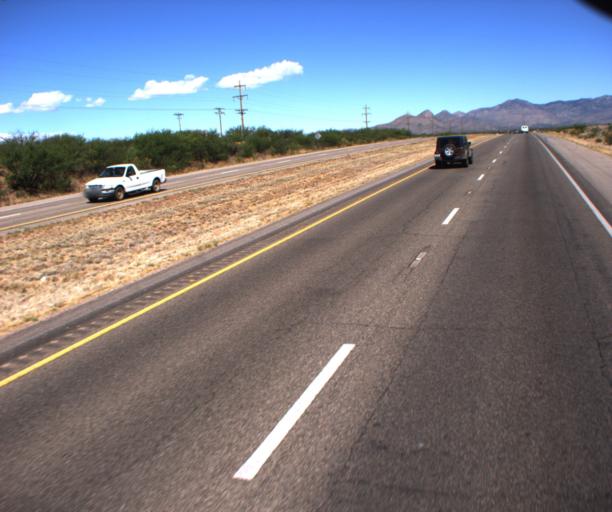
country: US
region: Arizona
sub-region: Cochise County
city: Huachuca City
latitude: 31.6521
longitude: -110.3438
